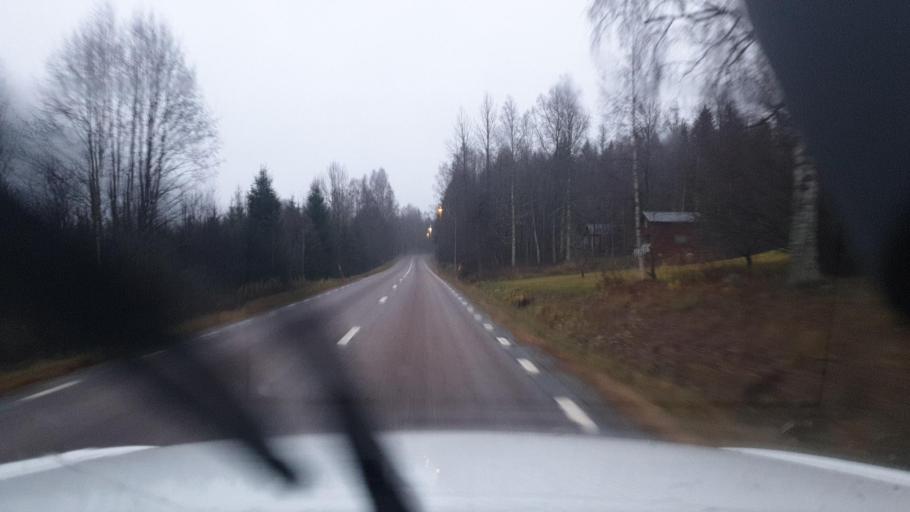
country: SE
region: Vaermland
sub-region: Sunne Kommun
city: Sunne
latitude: 59.8875
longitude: 12.9225
